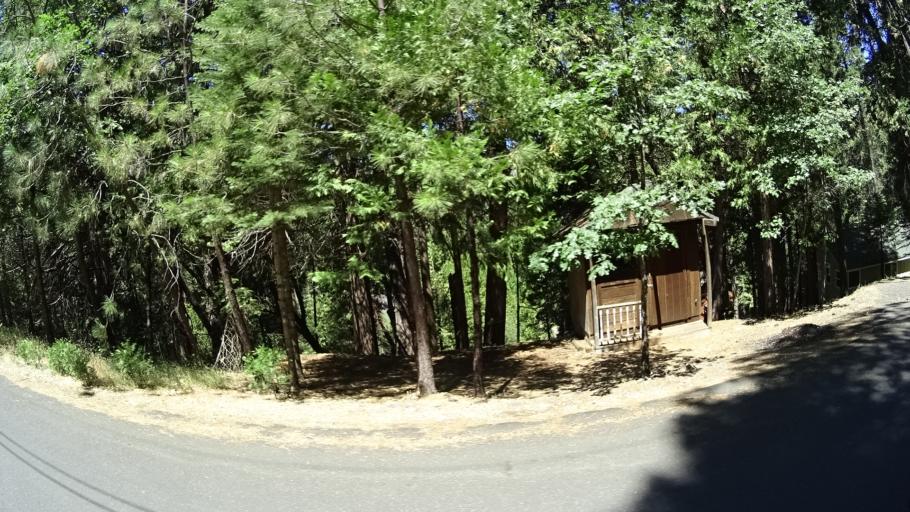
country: US
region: California
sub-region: Calaveras County
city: Arnold
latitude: 38.2328
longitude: -120.3441
